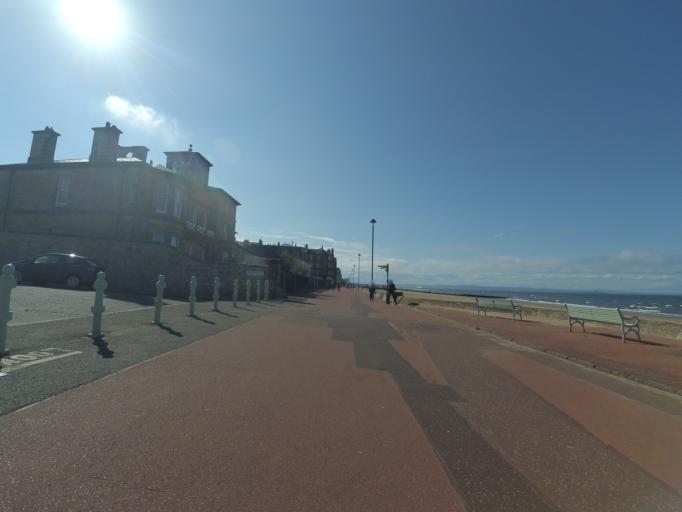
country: GB
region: Scotland
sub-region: West Lothian
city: Seafield
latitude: 55.9511
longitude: -3.1011
